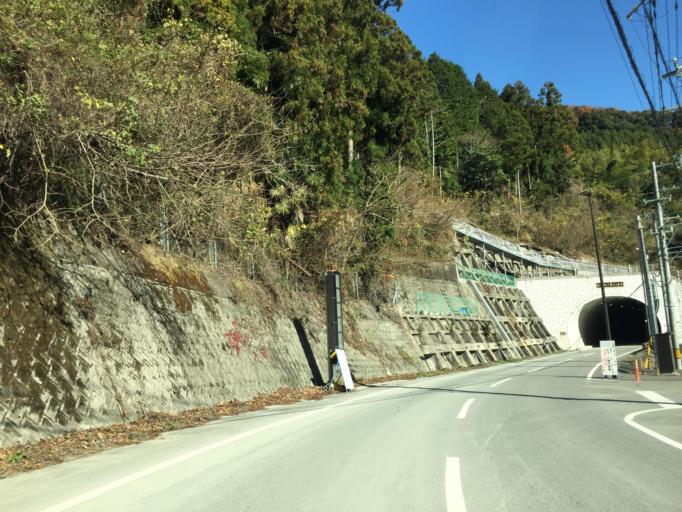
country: JP
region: Wakayama
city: Iwade
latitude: 34.1368
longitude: 135.3985
